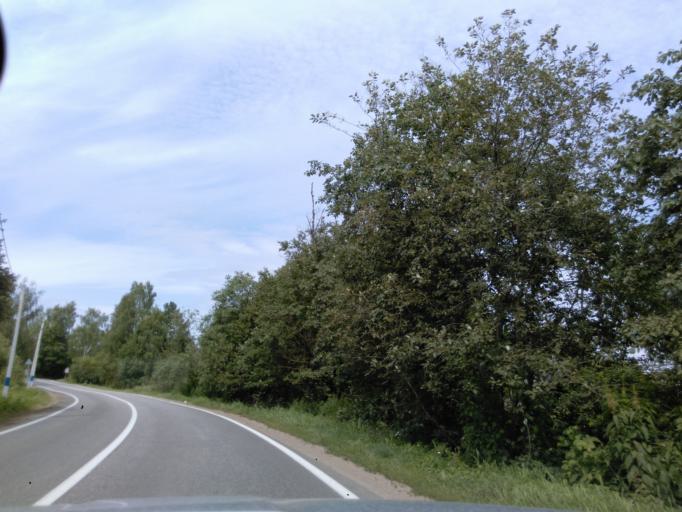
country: RU
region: Moskovskaya
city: Solnechnogorsk
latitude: 56.1624
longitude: 36.9778
